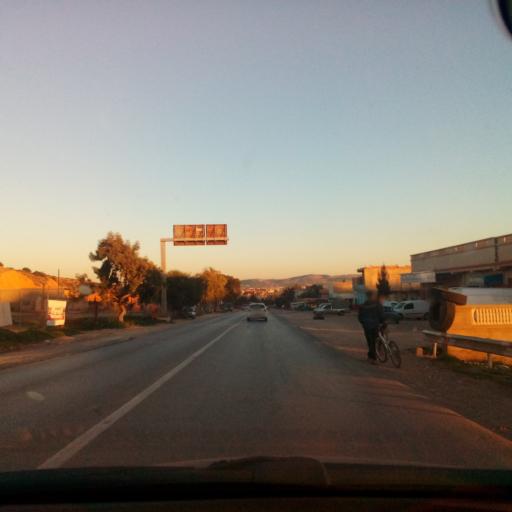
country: DZ
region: Relizane
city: Relizane
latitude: 35.7172
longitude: 0.3322
